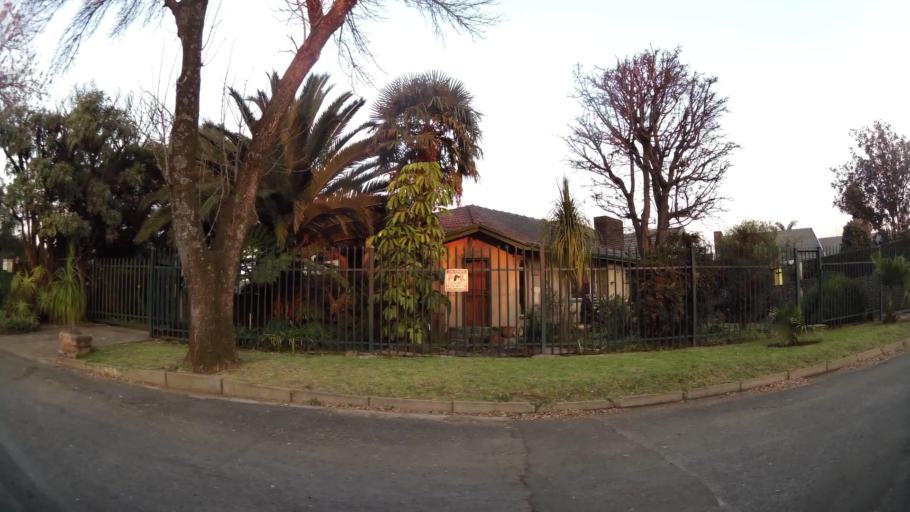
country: ZA
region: Gauteng
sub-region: Ekurhuleni Metropolitan Municipality
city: Tembisa
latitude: -26.0577
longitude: 28.2322
